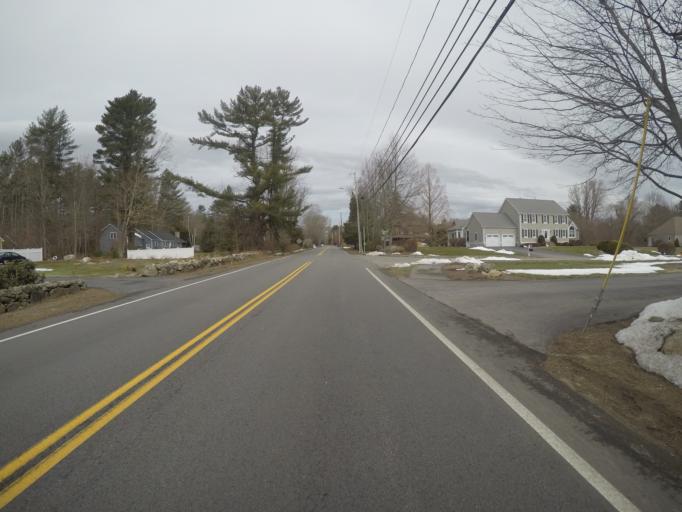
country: US
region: Massachusetts
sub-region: Bristol County
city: Easton
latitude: 42.0330
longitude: -71.1206
